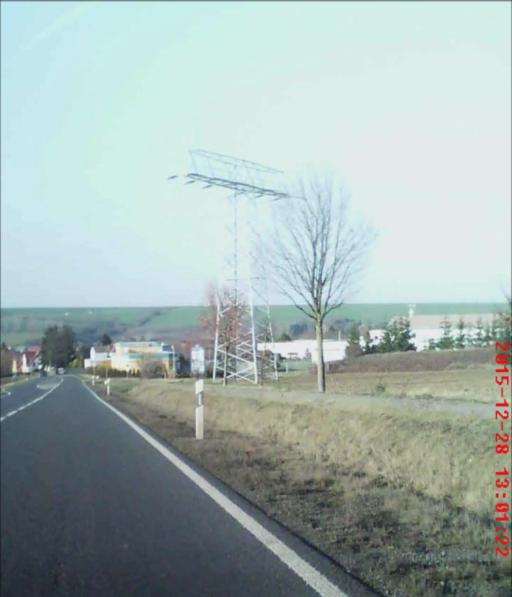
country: DE
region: Thuringia
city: Niederrossla
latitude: 51.0333
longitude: 11.4974
